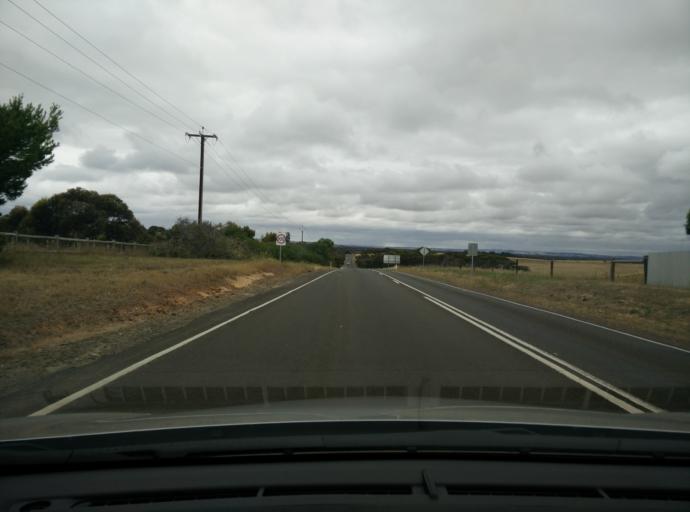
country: AU
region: South Australia
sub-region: Kangaroo Island
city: Kingscote
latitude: -35.6628
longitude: 137.5997
